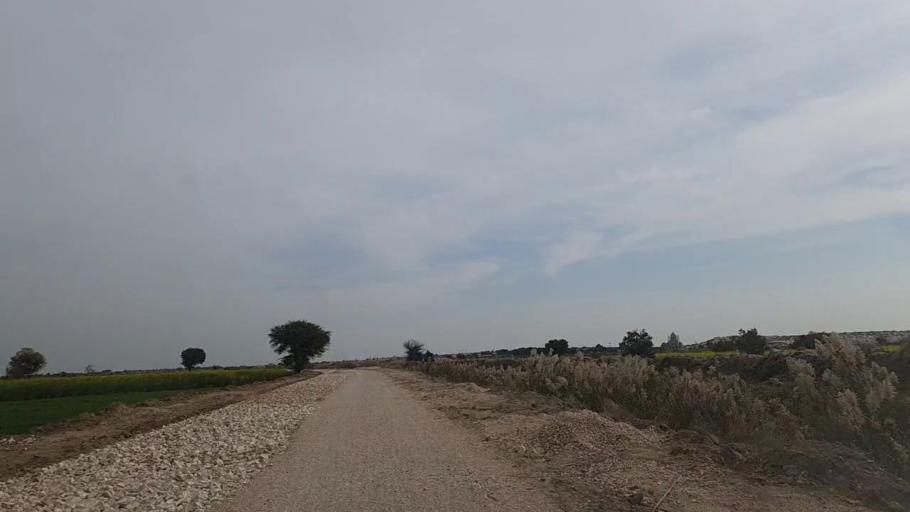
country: PK
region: Sindh
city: Jam Sahib
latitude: 26.4050
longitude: 68.4954
